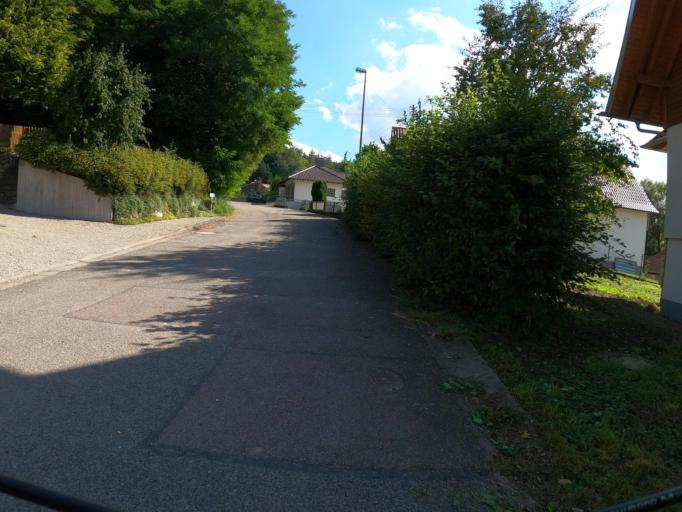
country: DE
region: Bavaria
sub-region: Swabia
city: Rieden an der Kotz
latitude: 48.3363
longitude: 10.2207
